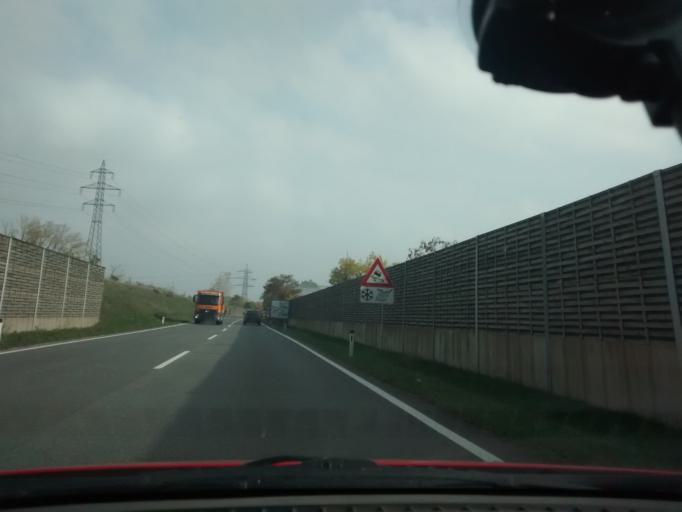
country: AT
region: Lower Austria
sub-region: Politischer Bezirk Modling
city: Biedermannsdorf
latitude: 48.0779
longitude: 16.3472
